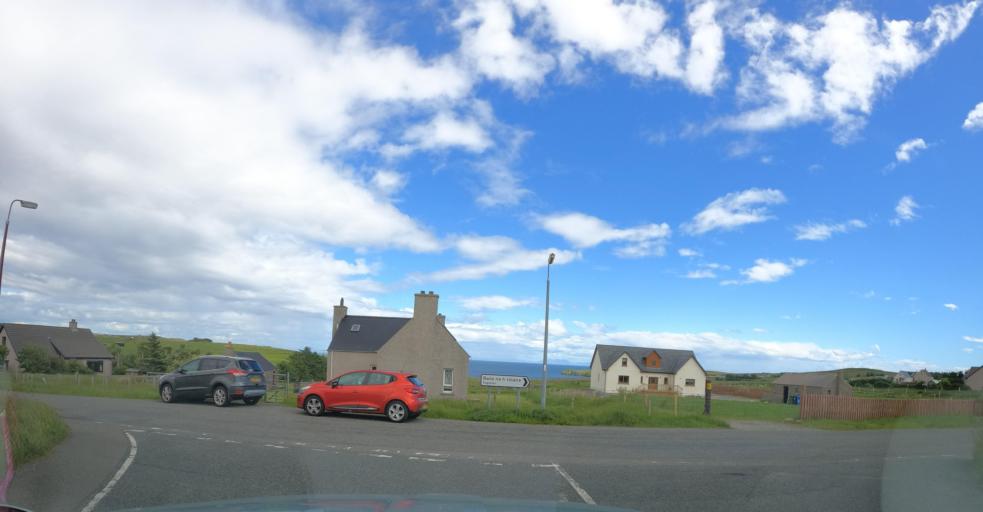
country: GB
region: Scotland
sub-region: Eilean Siar
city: Stornoway
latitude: 58.2002
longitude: -6.2243
